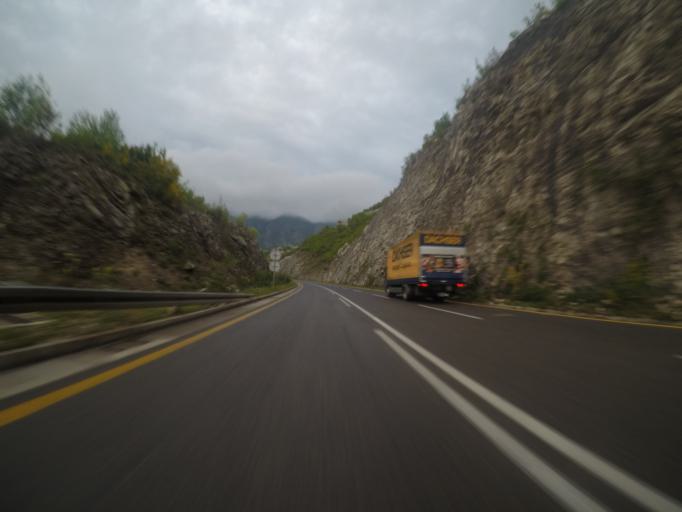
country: ME
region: Bar
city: Sutomore
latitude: 42.2134
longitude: 19.0483
